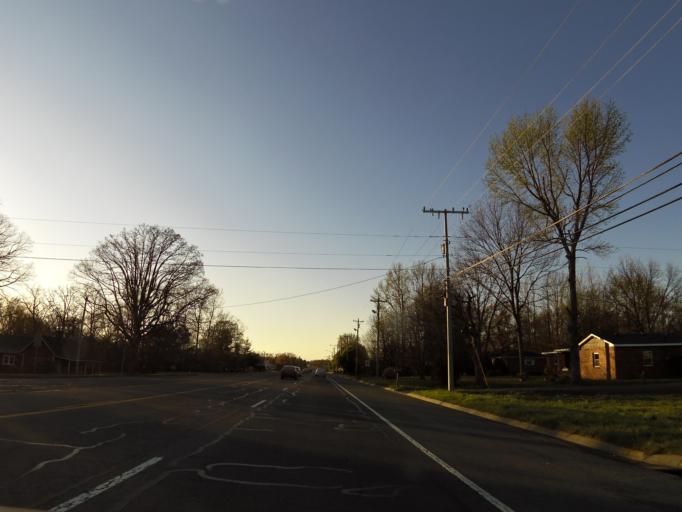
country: US
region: Tennessee
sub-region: Robertson County
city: Ridgetop
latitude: 36.4106
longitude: -86.7885
